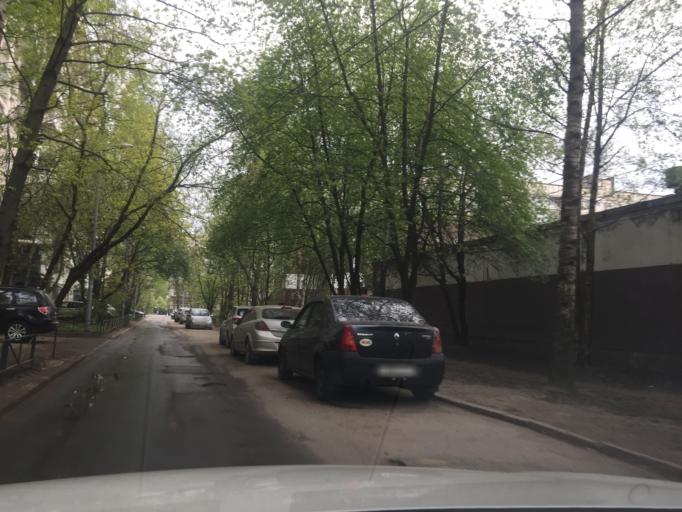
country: RU
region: Leningrad
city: Parnas
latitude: 60.0553
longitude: 30.3398
